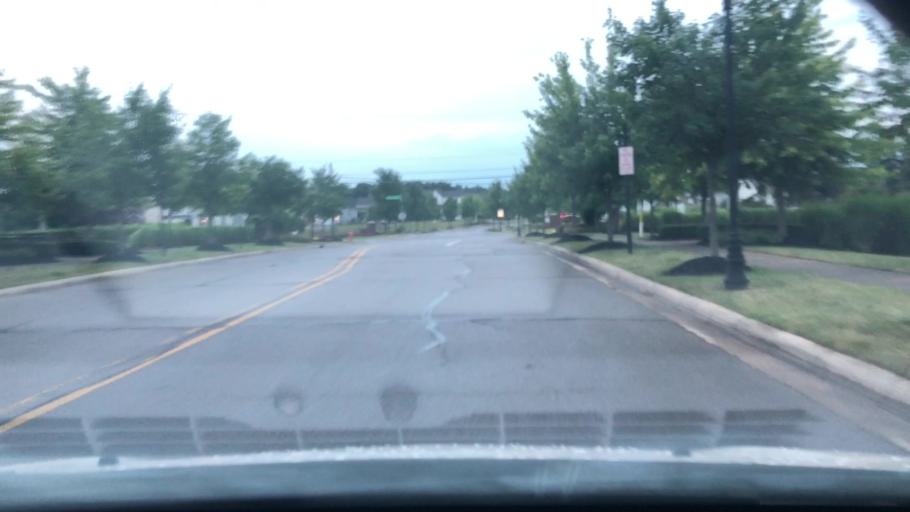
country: US
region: Ohio
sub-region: Franklin County
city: New Albany
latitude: 40.1011
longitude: -82.8544
